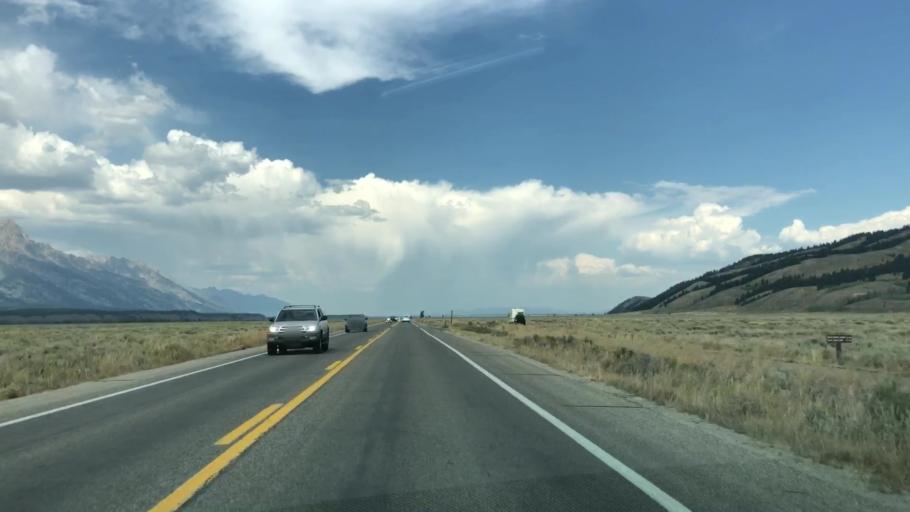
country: US
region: Wyoming
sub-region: Teton County
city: Jackson
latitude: 43.6122
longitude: -110.7223
